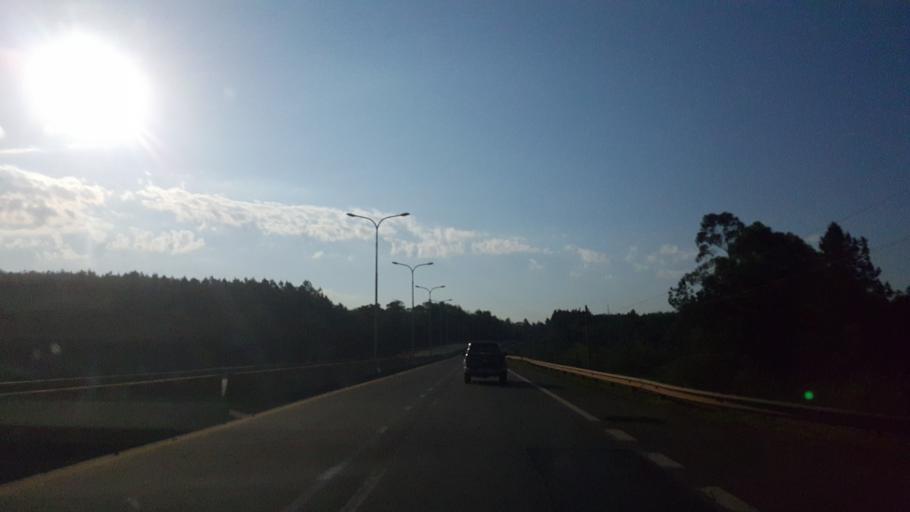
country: AR
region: Misiones
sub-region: Departamento de San Ignacio
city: San Ignacio
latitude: -27.2818
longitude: -55.5349
